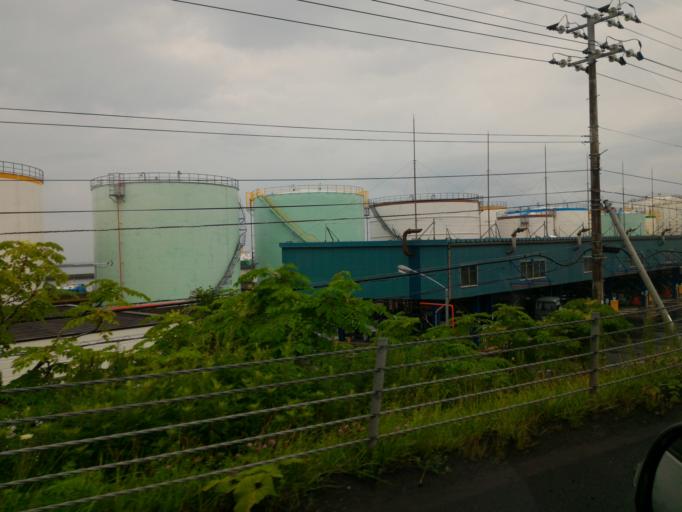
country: JP
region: Hokkaido
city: Rumoi
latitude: 43.9569
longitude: 141.6439
